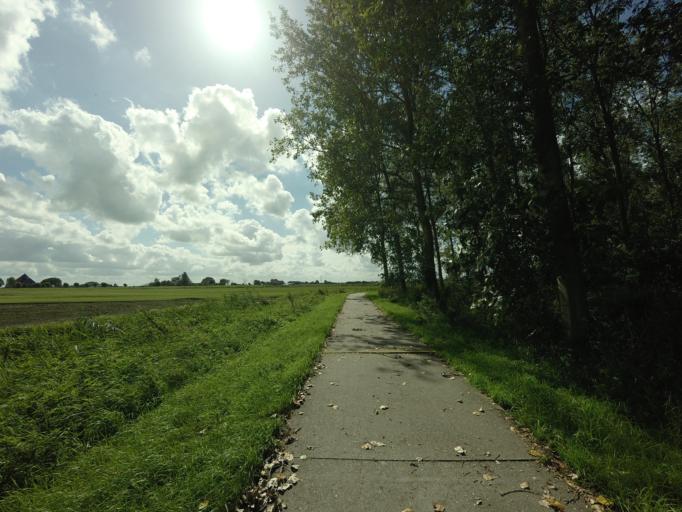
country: NL
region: North Holland
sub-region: Gemeente Purmerend
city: Purmerend
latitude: 52.4709
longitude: 4.9744
